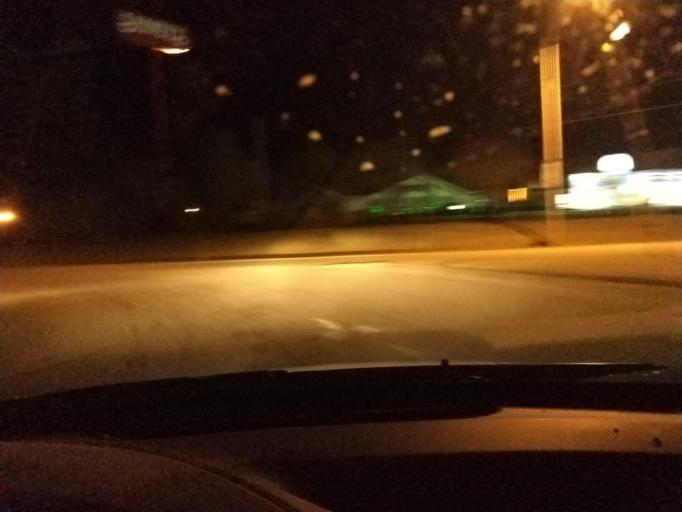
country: US
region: South Carolina
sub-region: Orangeburg County
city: Holly Hill
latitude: 33.4849
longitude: -80.4700
